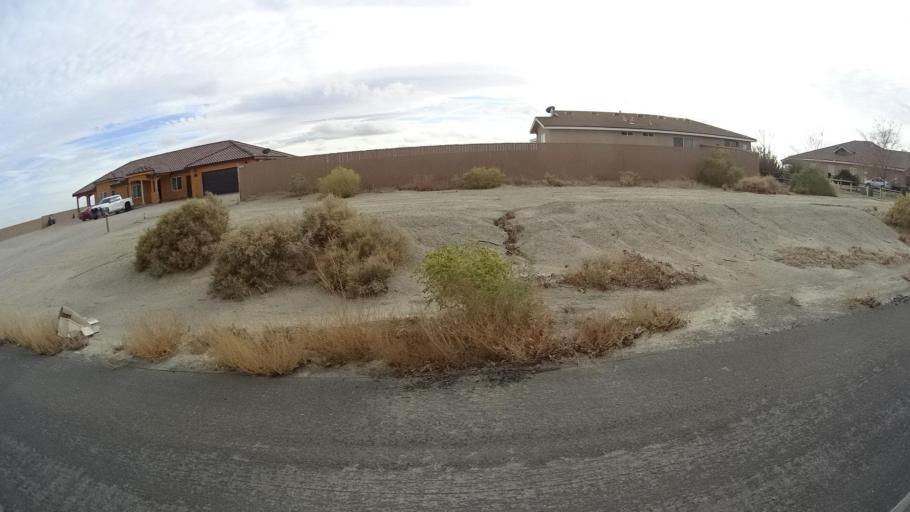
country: US
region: California
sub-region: Kern County
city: Rosamond
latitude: 34.8495
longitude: -118.1928
